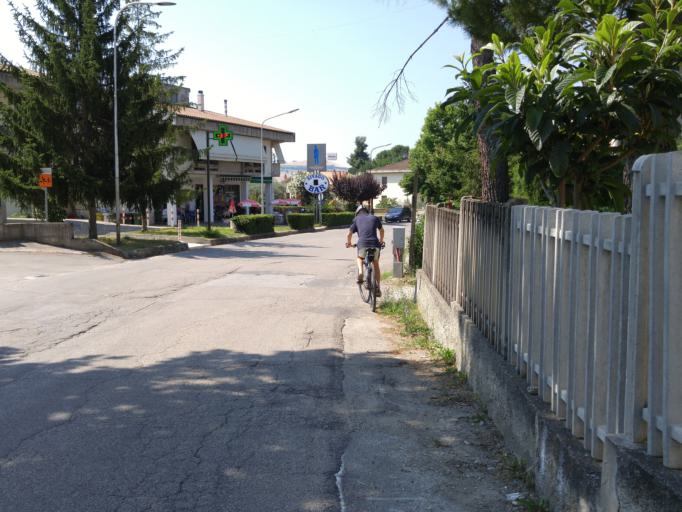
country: IT
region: Abruzzo
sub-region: Provincia di Teramo
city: Castilenti
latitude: 42.5352
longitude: 13.9200
